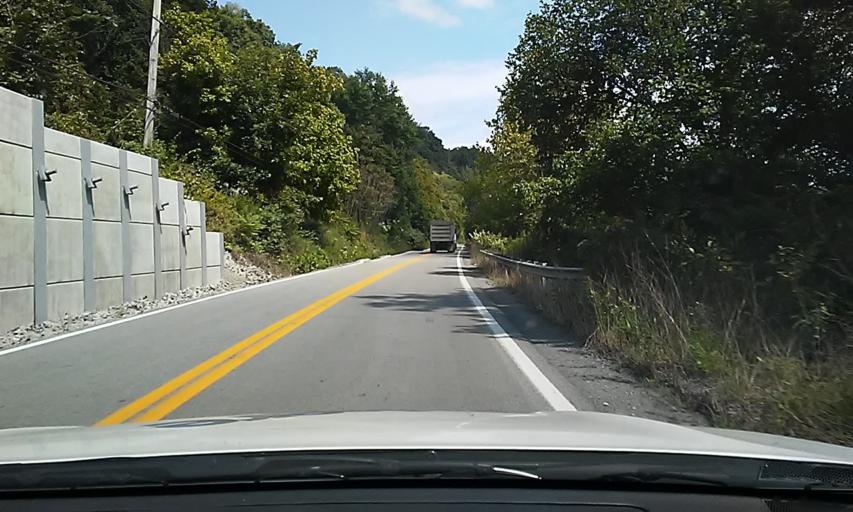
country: US
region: West Virginia
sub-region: Monongalia County
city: Star City
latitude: 39.6830
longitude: -79.9723
